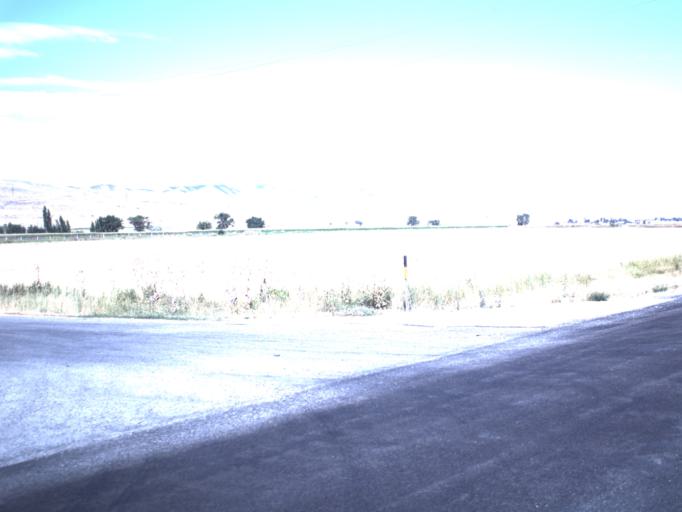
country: US
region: Utah
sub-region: Box Elder County
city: Garland
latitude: 41.7703
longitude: -112.1489
